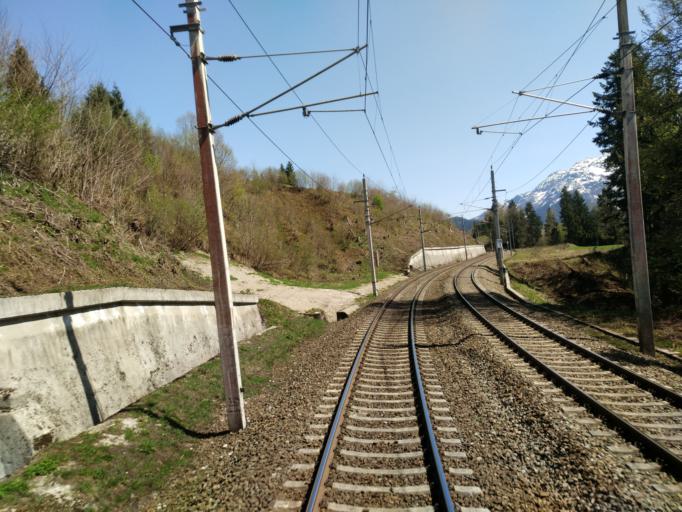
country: AT
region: Tyrol
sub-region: Politischer Bezirk Kitzbuhel
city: Fieberbrunn
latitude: 47.4750
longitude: 12.5576
